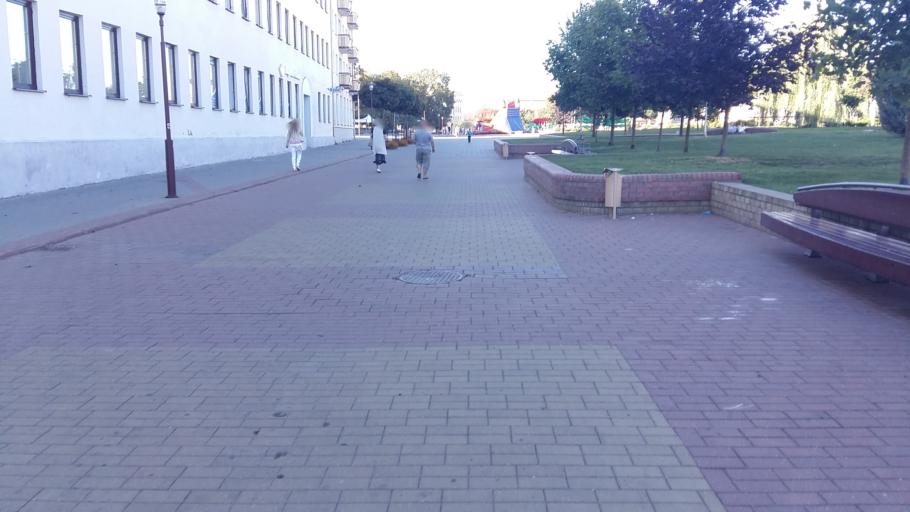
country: BY
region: Grodnenskaya
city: Hrodna
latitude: 53.6768
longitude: 23.8289
